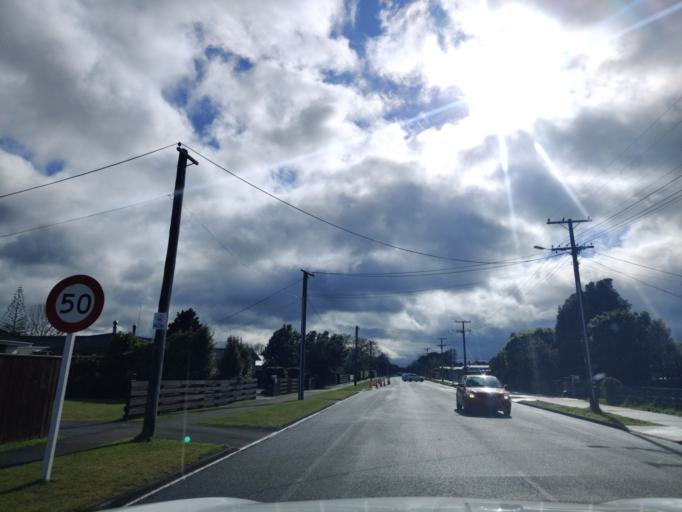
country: NZ
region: Manawatu-Wanganui
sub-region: Palmerston North City
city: Palmerston North
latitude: -40.2874
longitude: 175.7588
